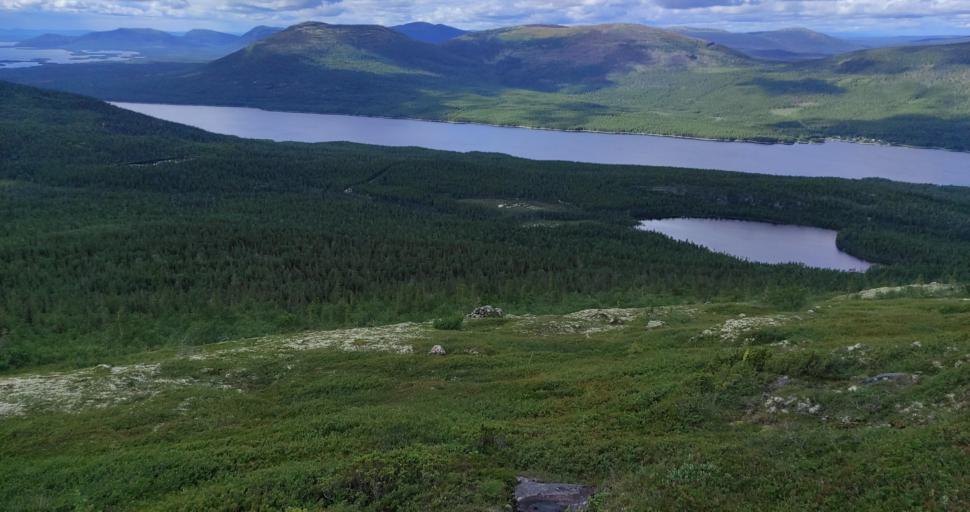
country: RU
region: Murmansk
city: Afrikanda
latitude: 67.0562
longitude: 32.9605
